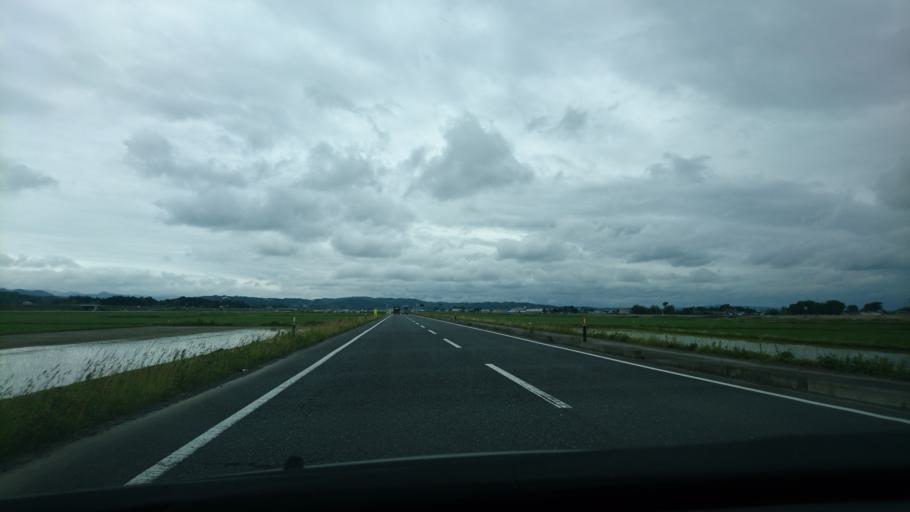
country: JP
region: Miyagi
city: Wakuya
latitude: 38.6834
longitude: 141.2610
